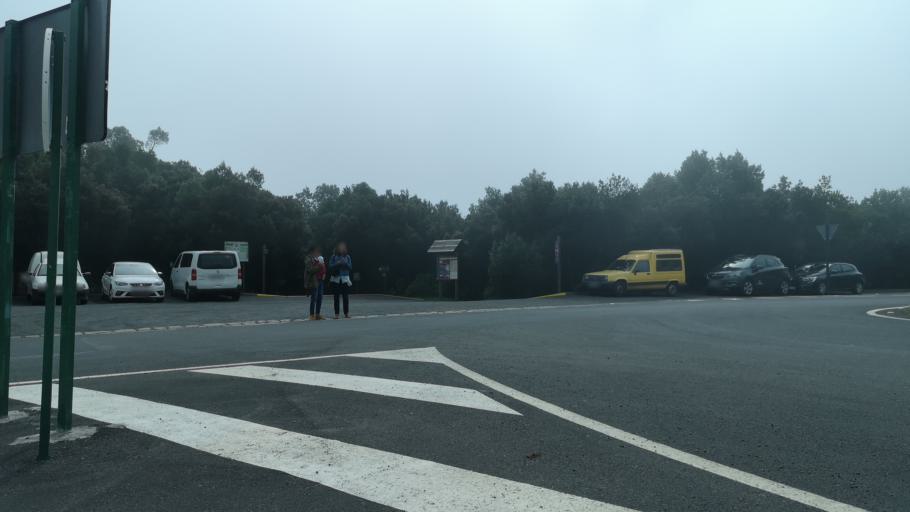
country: ES
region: Canary Islands
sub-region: Provincia de Santa Cruz de Tenerife
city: Alajero
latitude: 28.1085
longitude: -17.2417
